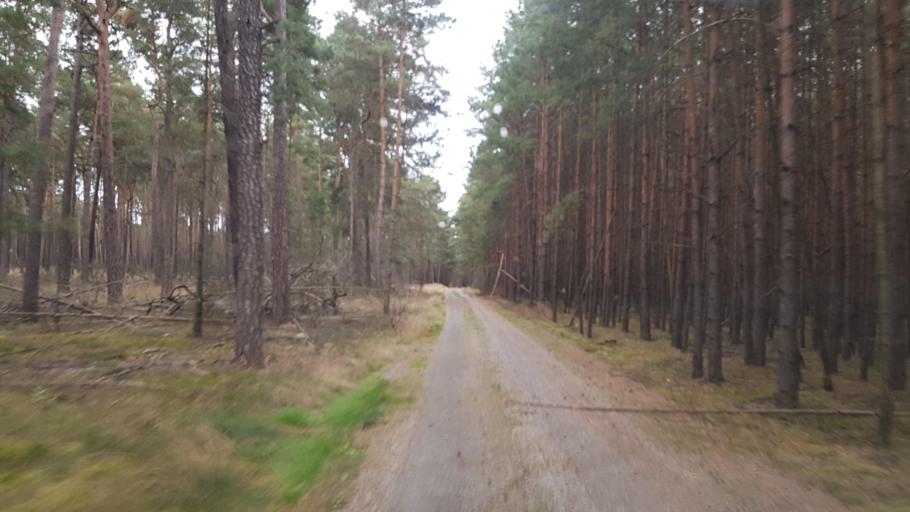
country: DE
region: Brandenburg
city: Sonnewalde
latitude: 51.7406
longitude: 13.6560
